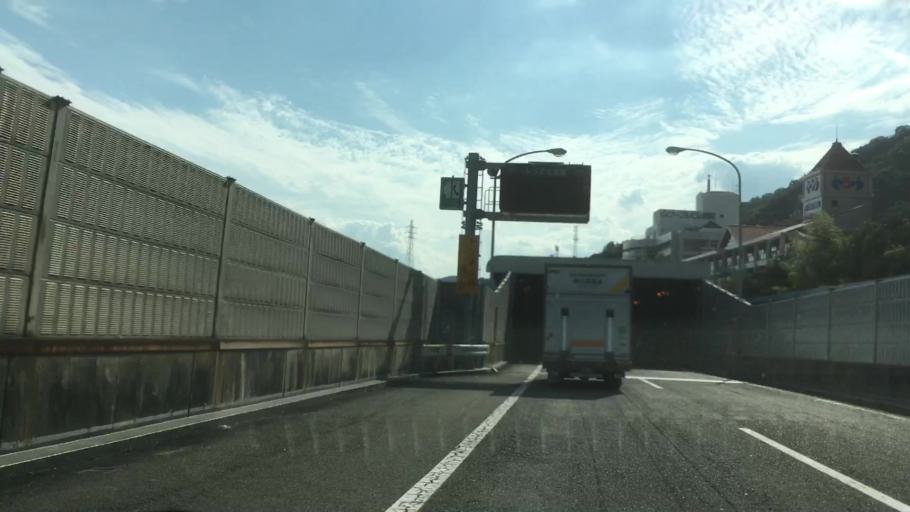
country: JP
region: Hiroshima
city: Ono-hara
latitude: 34.2582
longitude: 132.2251
